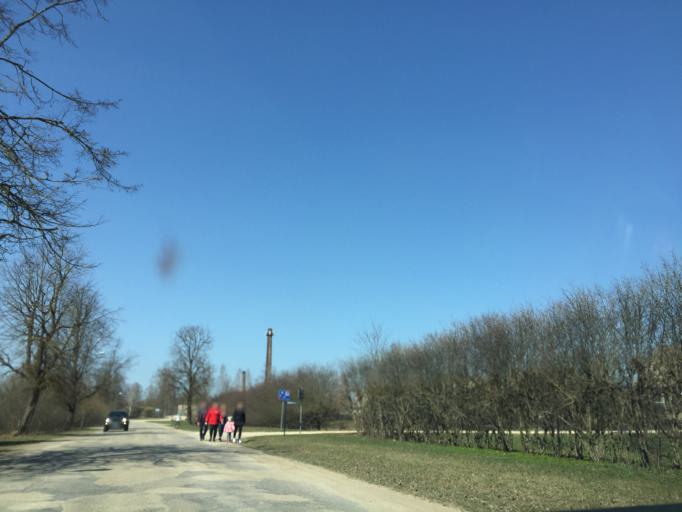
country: LV
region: Malpils
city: Malpils
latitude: 57.0092
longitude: 24.9645
